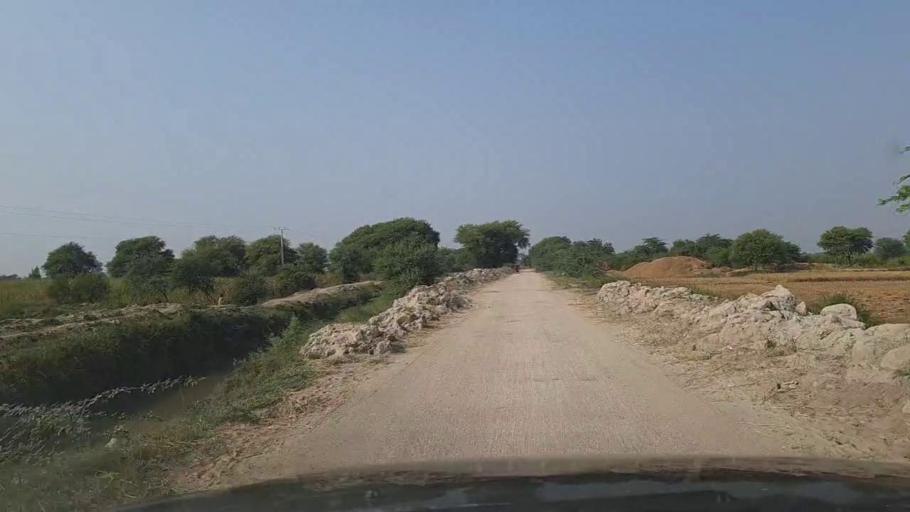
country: PK
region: Sindh
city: Mirpur Batoro
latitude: 24.7023
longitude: 68.2559
